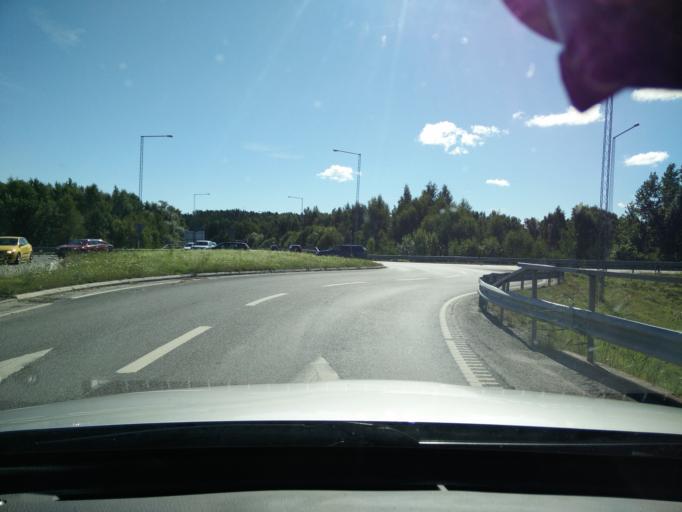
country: SE
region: Stockholm
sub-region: Taby Kommun
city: Taby
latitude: 59.4558
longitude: 18.1362
